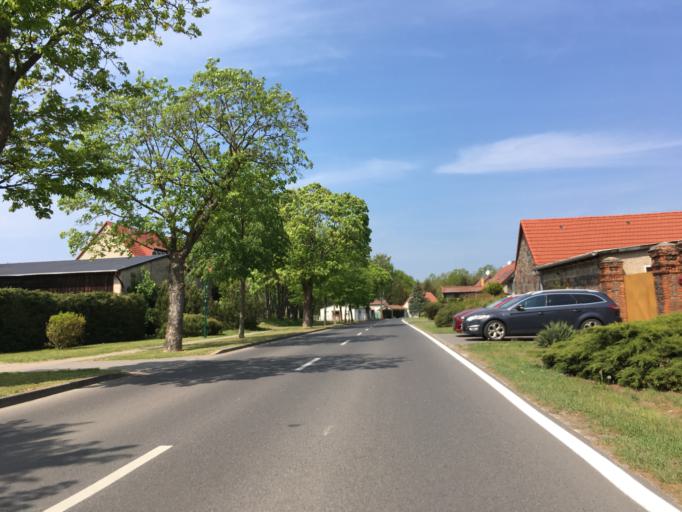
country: DE
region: Brandenburg
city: Melchow
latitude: 52.7111
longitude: 13.7164
